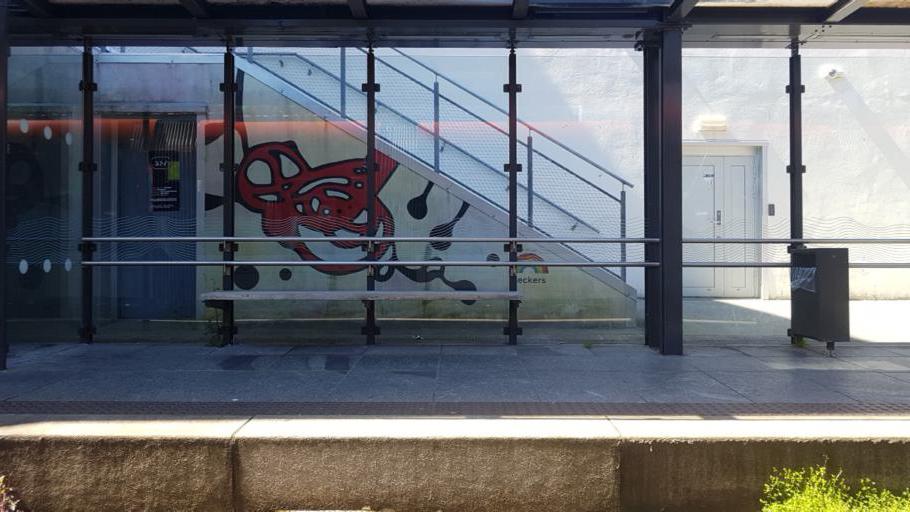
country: NO
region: Hordaland
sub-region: Bergen
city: Bergen
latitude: 60.3459
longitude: 5.3526
